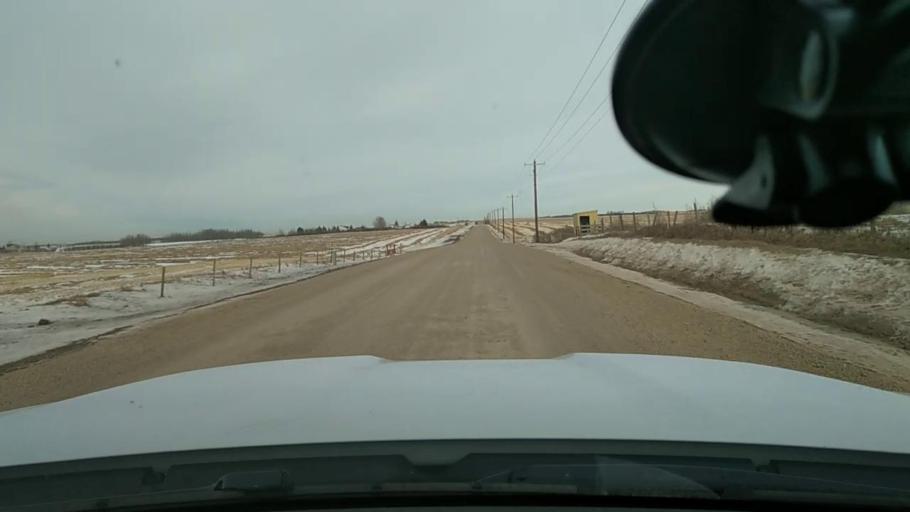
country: CA
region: Alberta
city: Airdrie
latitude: 51.2262
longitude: -113.9118
